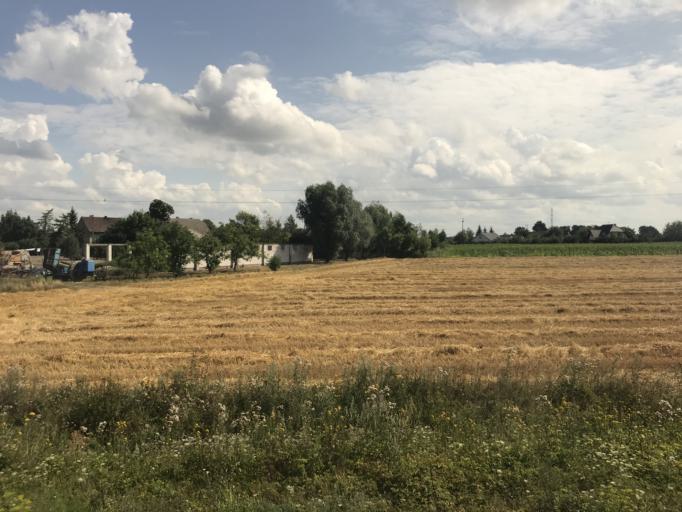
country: PL
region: Kujawsko-Pomorskie
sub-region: Powiat inowroclawski
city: Zlotniki Kujawskie
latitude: 52.8993
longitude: 18.1521
